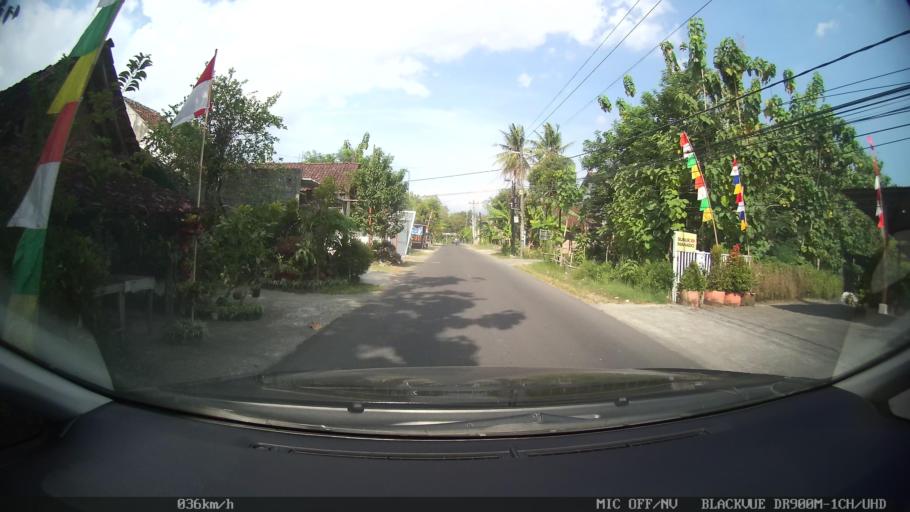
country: ID
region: Daerah Istimewa Yogyakarta
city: Kasihan
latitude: -7.8415
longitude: 110.3082
